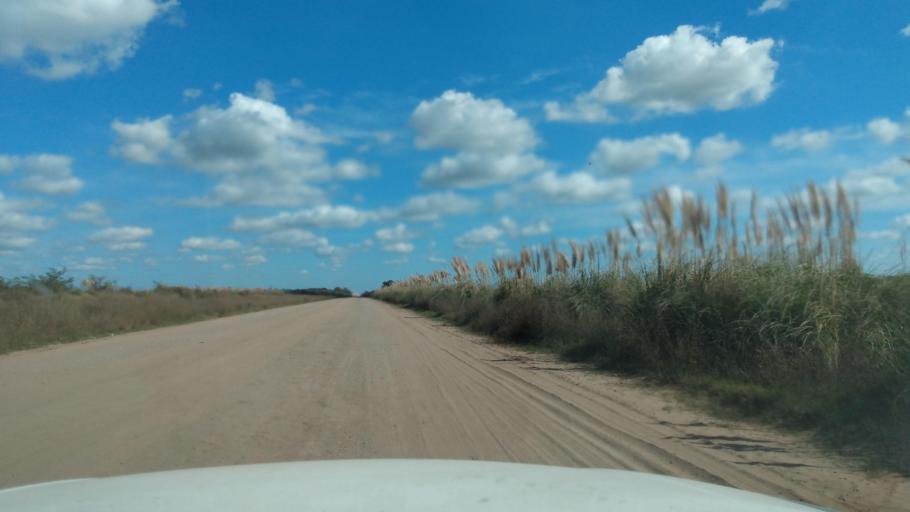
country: AR
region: Buenos Aires
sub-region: Partido de Navarro
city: Navarro
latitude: -35.0038
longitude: -59.3674
